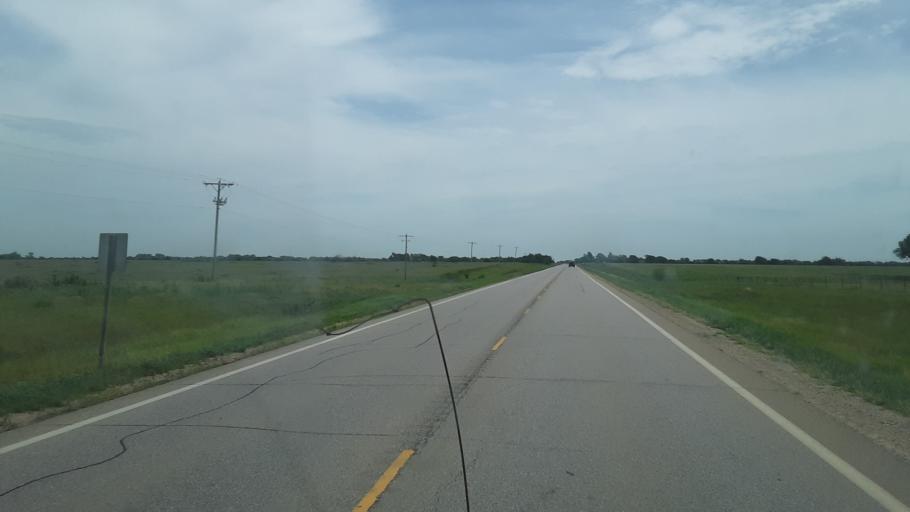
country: US
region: Kansas
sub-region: Butler County
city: El Dorado
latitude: 37.8107
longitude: -96.6980
